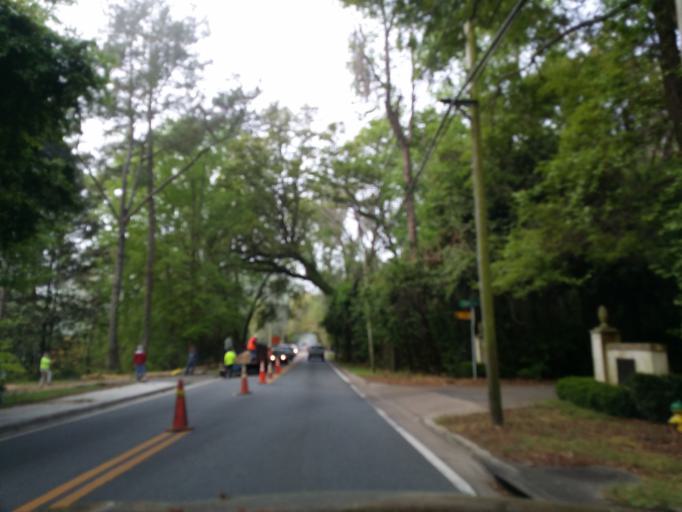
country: US
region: Florida
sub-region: Leon County
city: Tallahassee
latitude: 30.4701
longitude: -84.2490
